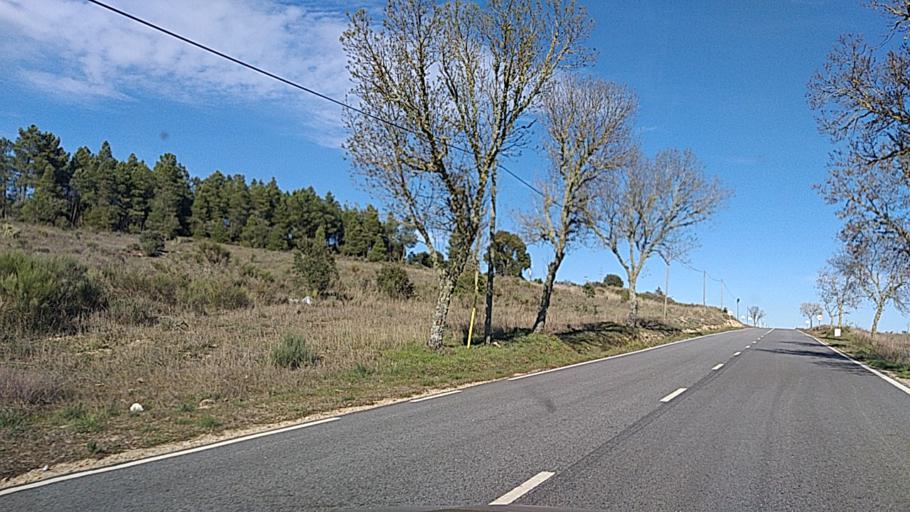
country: ES
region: Castille and Leon
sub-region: Provincia de Salamanca
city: Fuentes de Onoro
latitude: 40.5996
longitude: -6.9554
